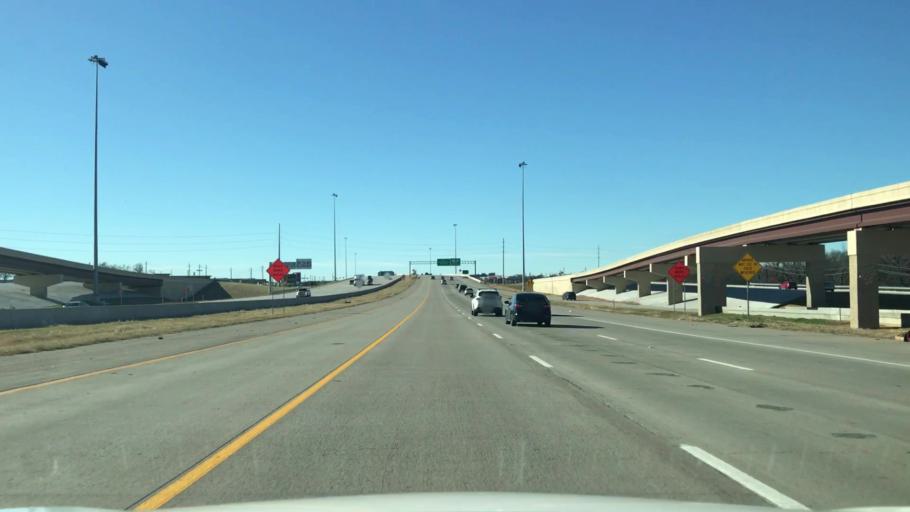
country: US
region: Texas
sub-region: Dallas County
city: Coppell
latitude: 32.9778
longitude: -97.0237
